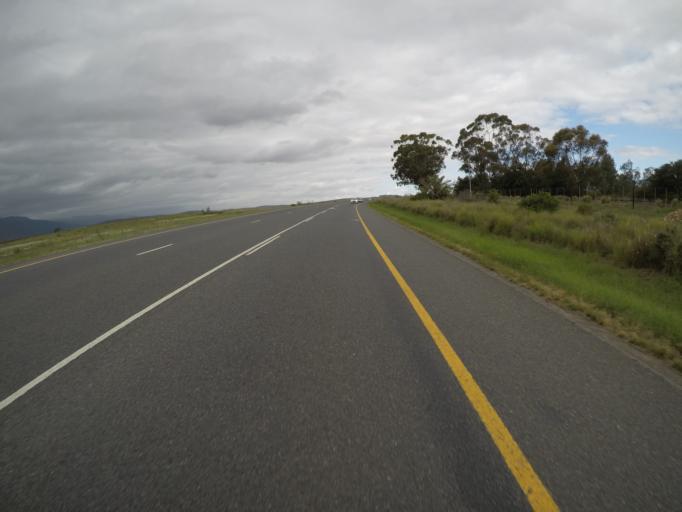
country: ZA
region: Western Cape
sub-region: Overberg District Municipality
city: Swellendam
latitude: -34.0425
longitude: 20.5676
